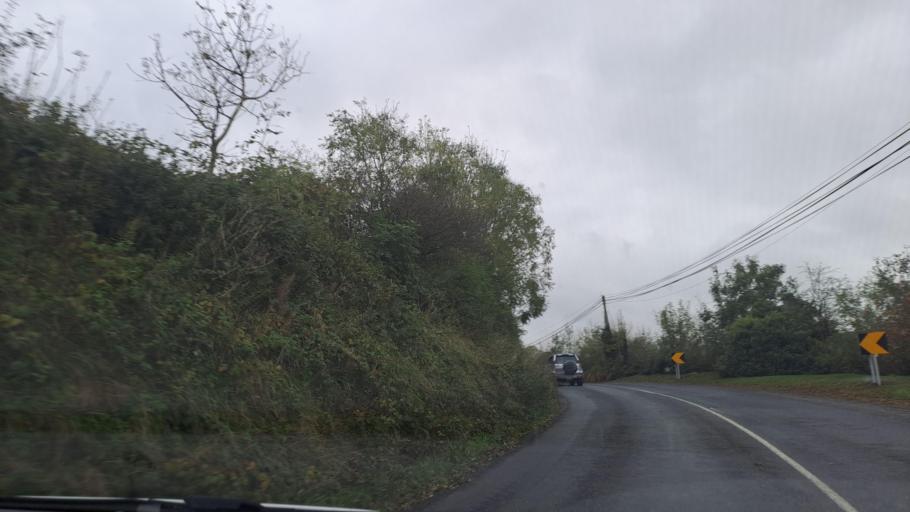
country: IE
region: Ulster
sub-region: An Cabhan
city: Bailieborough
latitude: 53.9608
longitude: -7.0403
